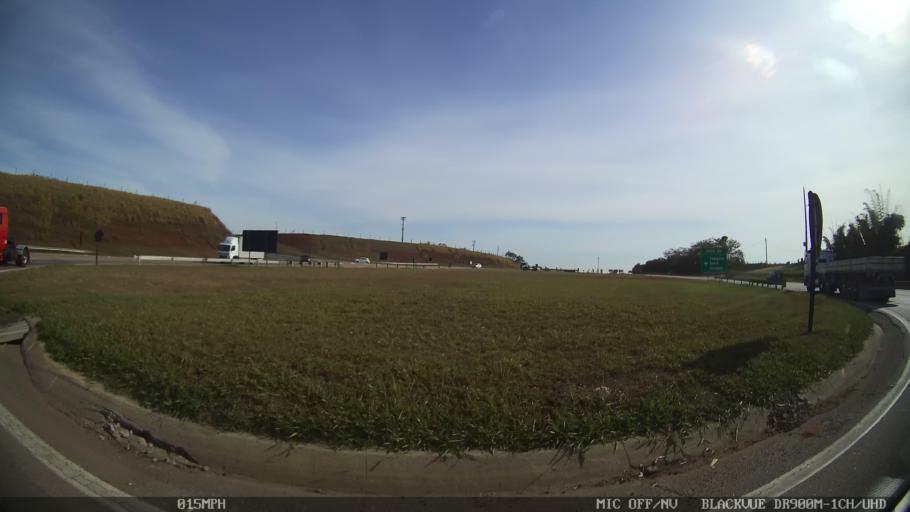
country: BR
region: Sao Paulo
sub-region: Rio Das Pedras
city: Rio das Pedras
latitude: -22.7945
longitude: -47.5812
